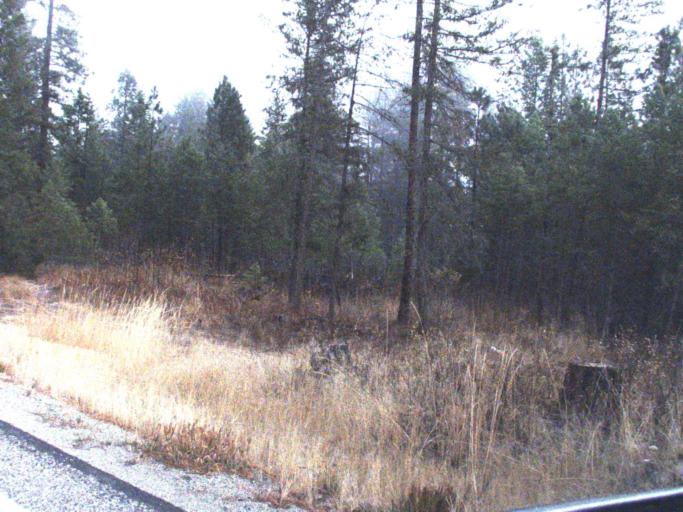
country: US
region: Washington
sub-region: Stevens County
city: Kettle Falls
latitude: 48.8481
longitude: -118.2000
